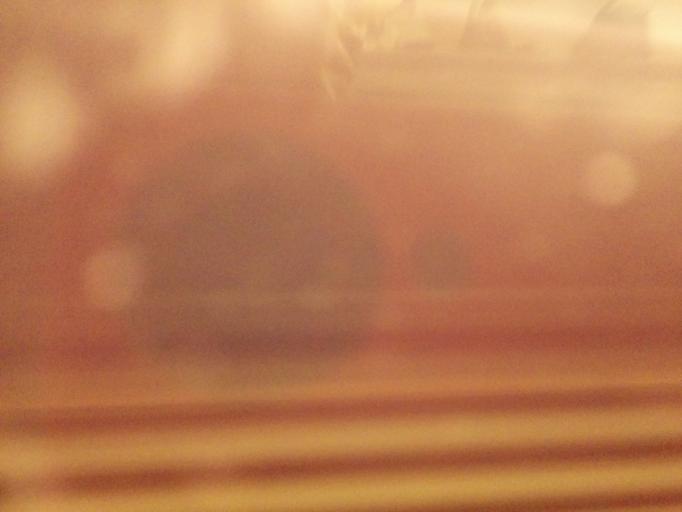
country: JP
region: Kanagawa
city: Odawara
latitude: 35.1983
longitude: 139.1353
